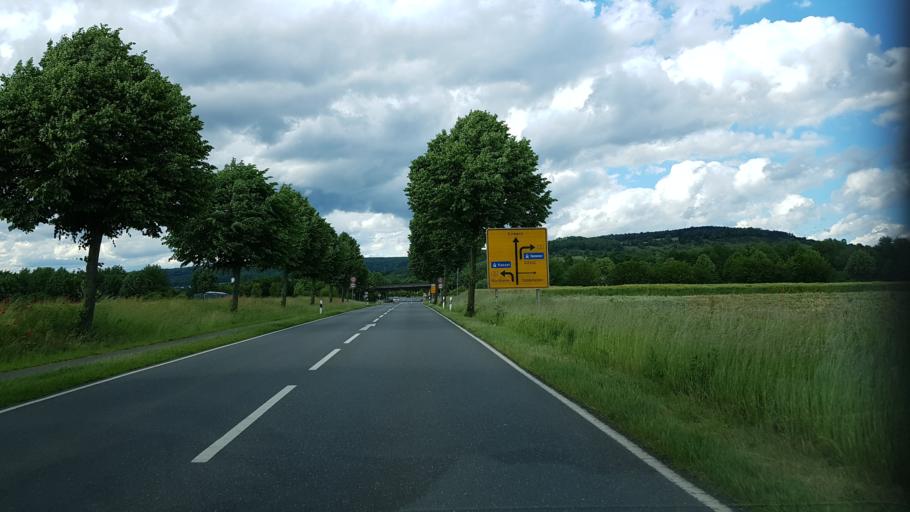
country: DE
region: Lower Saxony
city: Einbeck
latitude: 51.8021
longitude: 9.8980
